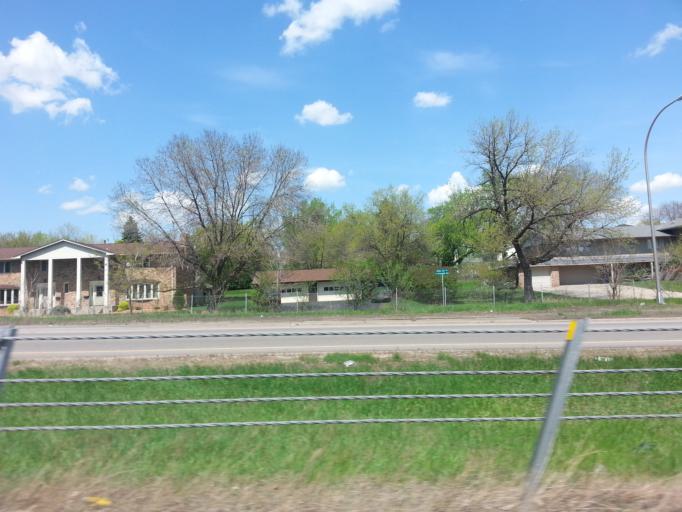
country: US
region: Minnesota
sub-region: Hennepin County
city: Edina
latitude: 44.8869
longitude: -93.3315
